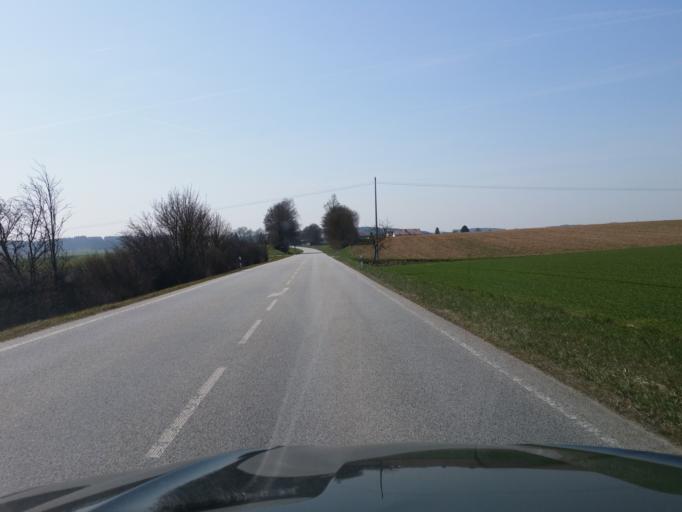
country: DE
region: Bavaria
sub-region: Lower Bavaria
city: Altfraunhofen
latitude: 48.4636
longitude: 12.1512
